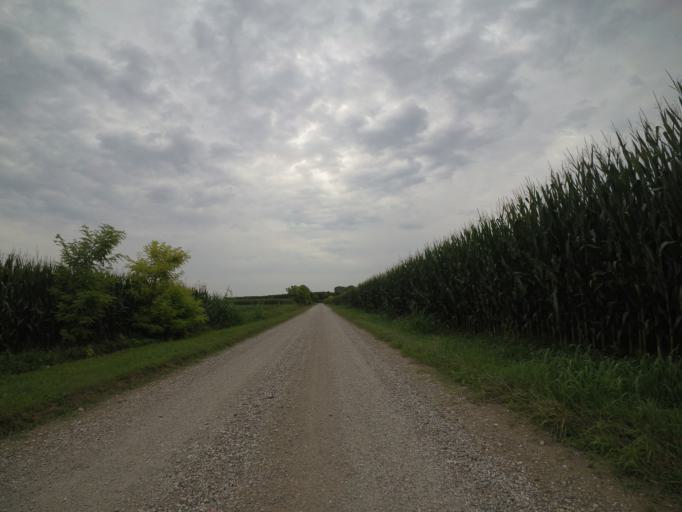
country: IT
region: Friuli Venezia Giulia
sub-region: Provincia di Udine
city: Varmo
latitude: 45.8729
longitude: 13.0101
